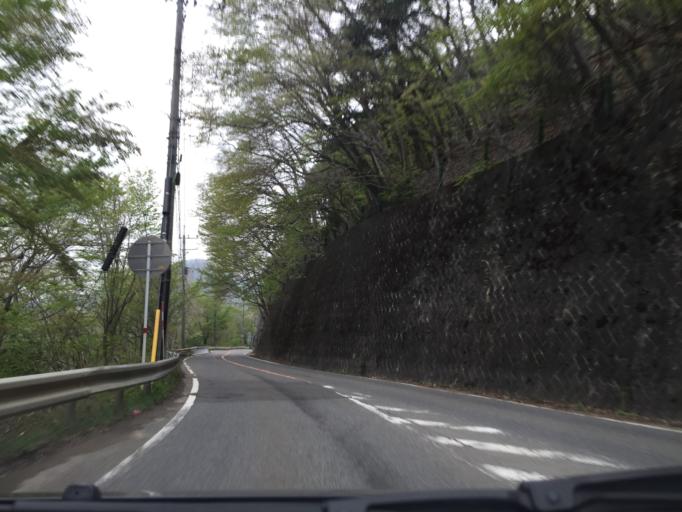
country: JP
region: Tochigi
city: Nikko
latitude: 36.9410
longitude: 139.6981
